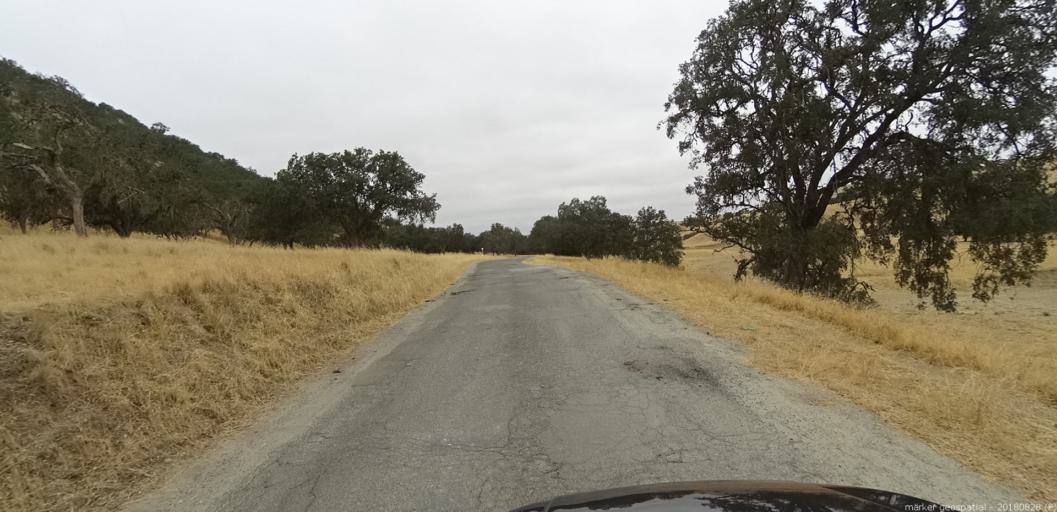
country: US
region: California
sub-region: San Luis Obispo County
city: Lake Nacimiento
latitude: 35.9503
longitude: -120.8172
